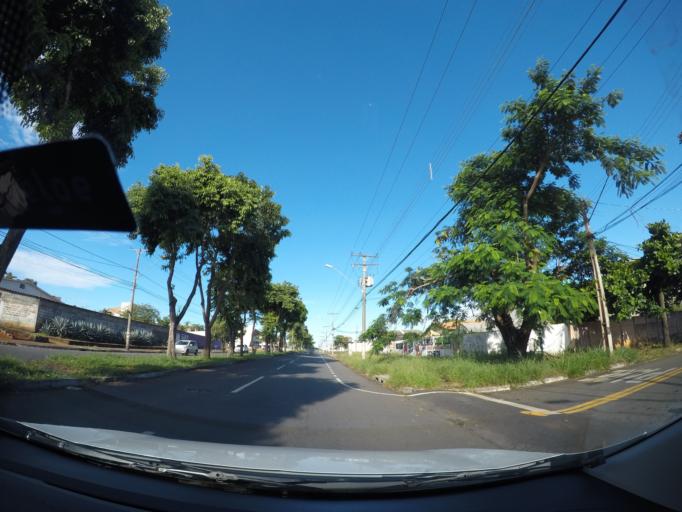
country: BR
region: Goias
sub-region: Goiania
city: Goiania
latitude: -16.7334
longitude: -49.3014
